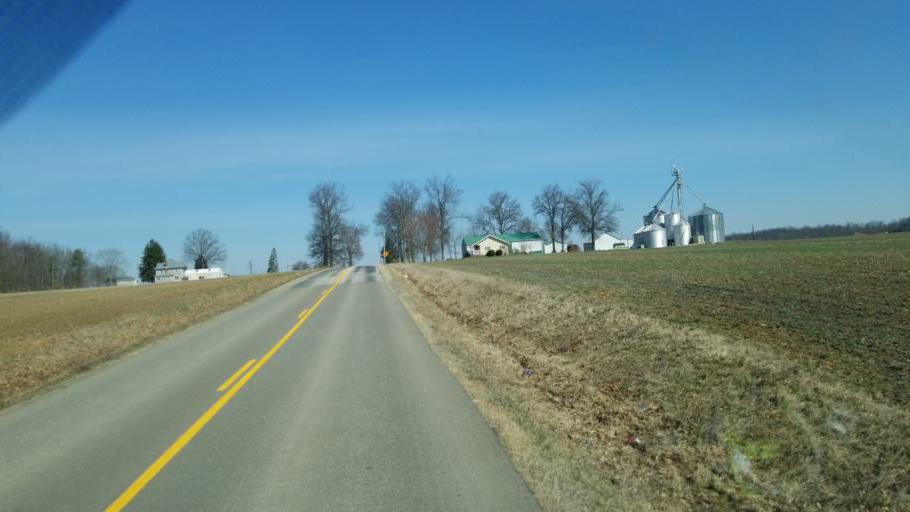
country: US
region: Ohio
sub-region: Ashland County
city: Ashland
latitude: 40.9202
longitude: -82.2432
